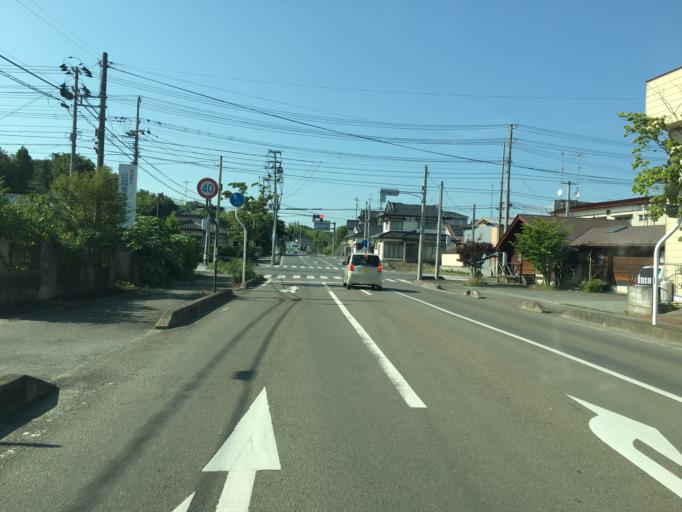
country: JP
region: Miyagi
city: Marumori
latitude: 37.7919
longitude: 140.9117
